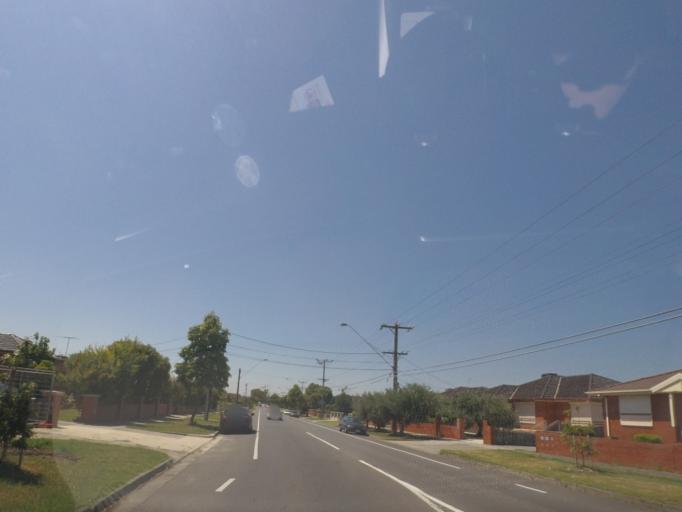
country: AU
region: Victoria
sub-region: Darebin
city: Reservoir
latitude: -37.7071
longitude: 144.9901
